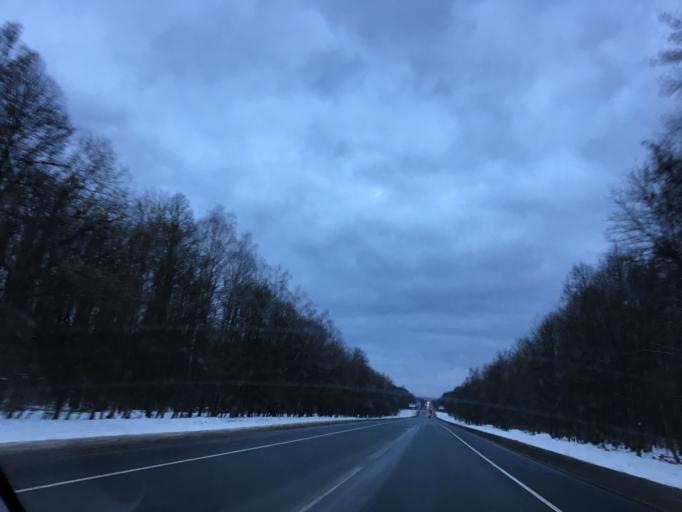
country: RU
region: Tula
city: Gorelki
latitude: 54.2804
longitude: 37.5893
